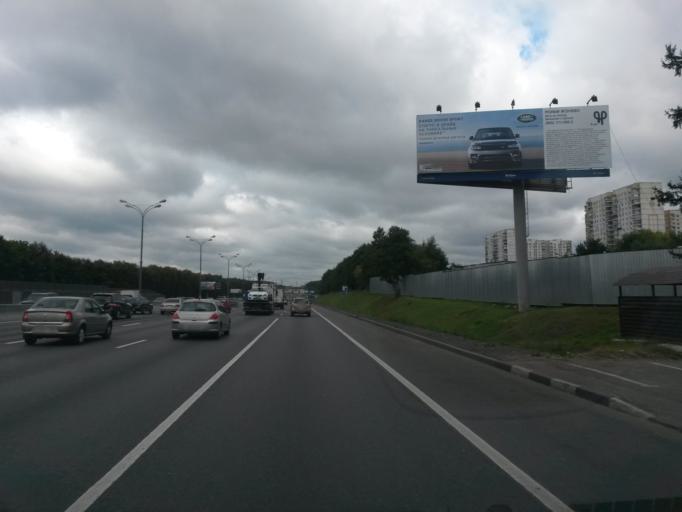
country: RU
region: Moscow
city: Yasenevo
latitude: 55.5885
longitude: 37.5425
